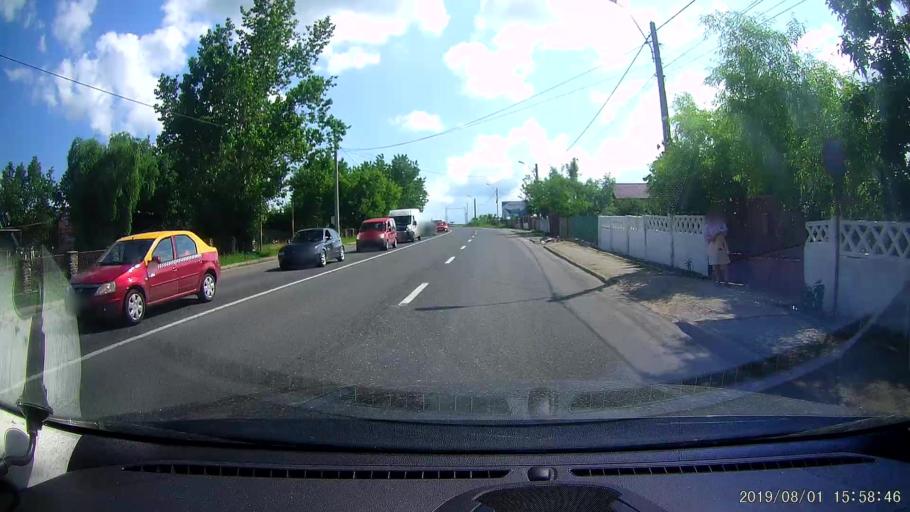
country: RO
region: Ialomita
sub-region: Comuna Slobozia
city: Slobozia
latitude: 44.5601
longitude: 27.3817
